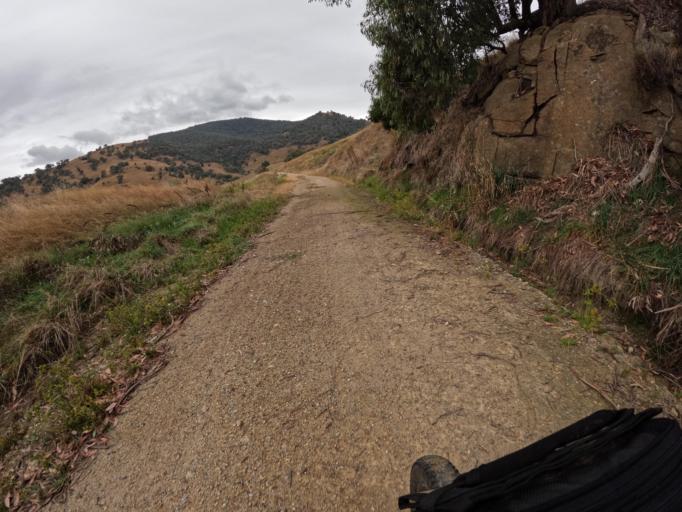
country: AU
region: New South Wales
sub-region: Albury Municipality
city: East Albury
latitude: -36.1836
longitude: 147.3678
